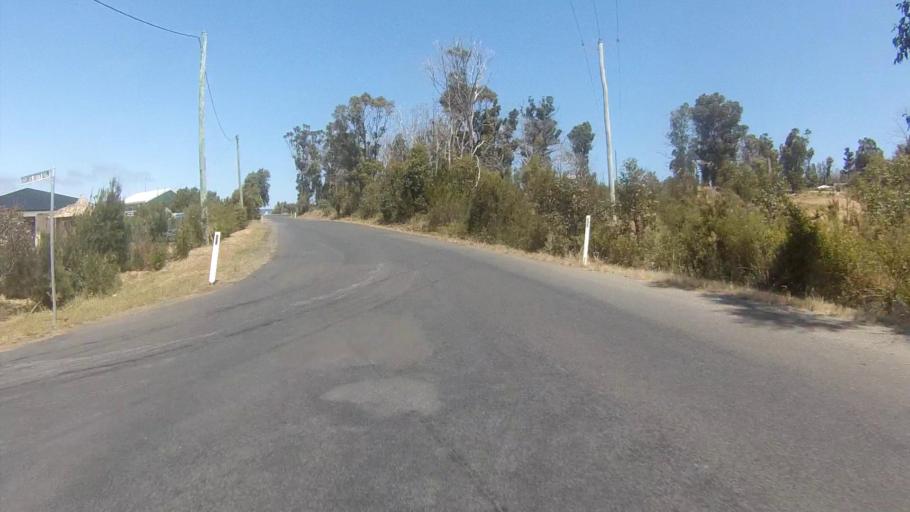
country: AU
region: Tasmania
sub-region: Sorell
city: Sorell
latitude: -42.8710
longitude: 147.8263
